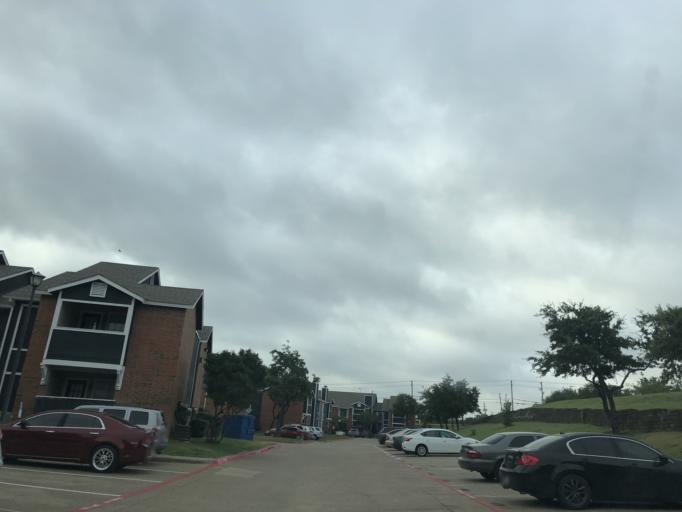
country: US
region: Texas
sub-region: Dallas County
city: Garland
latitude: 32.8389
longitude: -96.6306
